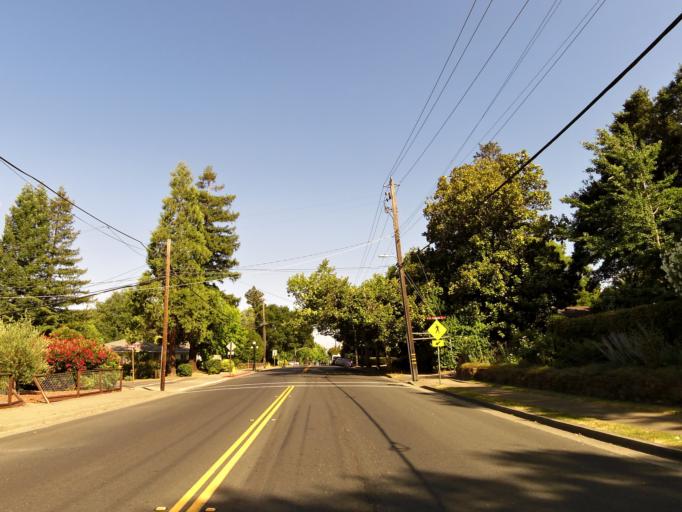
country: US
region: California
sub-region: Napa County
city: Saint Helena
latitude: 38.5081
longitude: -122.4751
